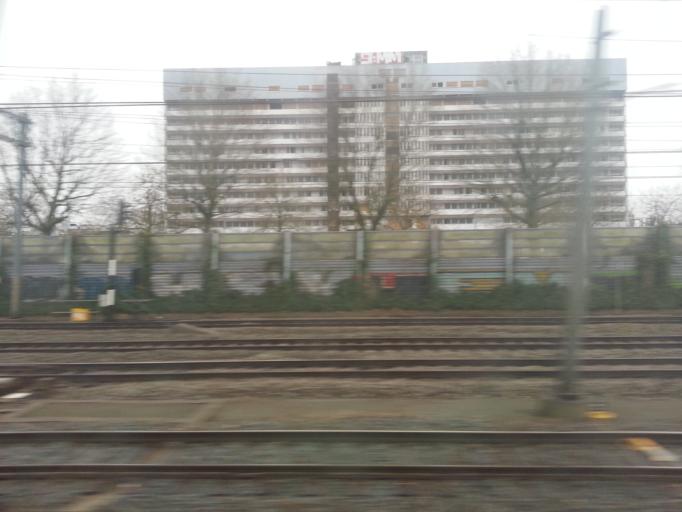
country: NL
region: South Holland
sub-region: Gemeente Barendrecht
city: Barendrecht
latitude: 51.8870
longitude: 4.5248
